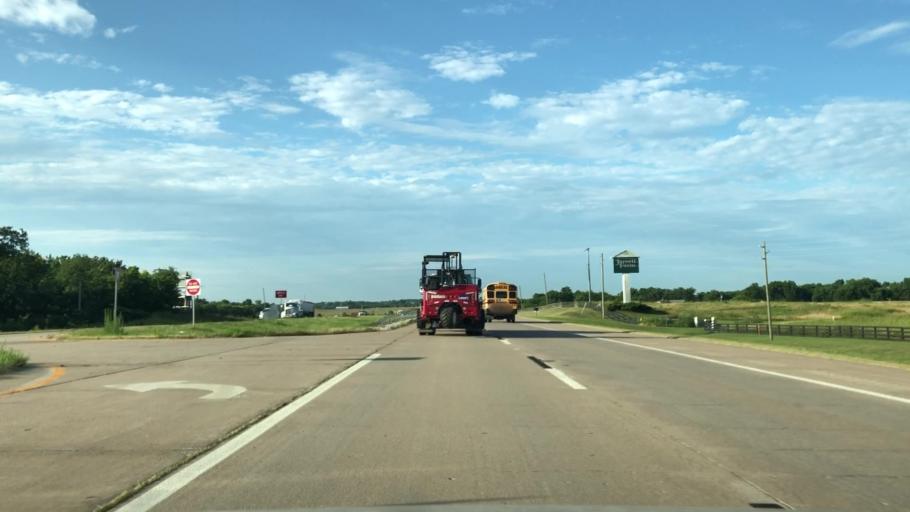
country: US
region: Oklahoma
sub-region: Osage County
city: Skiatook
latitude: 36.4600
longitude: -95.9207
